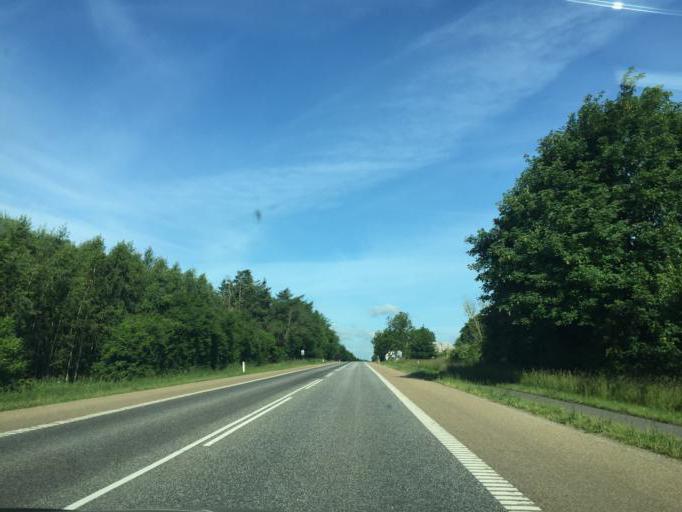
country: DK
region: South Denmark
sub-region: Middelfart Kommune
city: Strib
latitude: 55.4928
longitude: 9.7873
